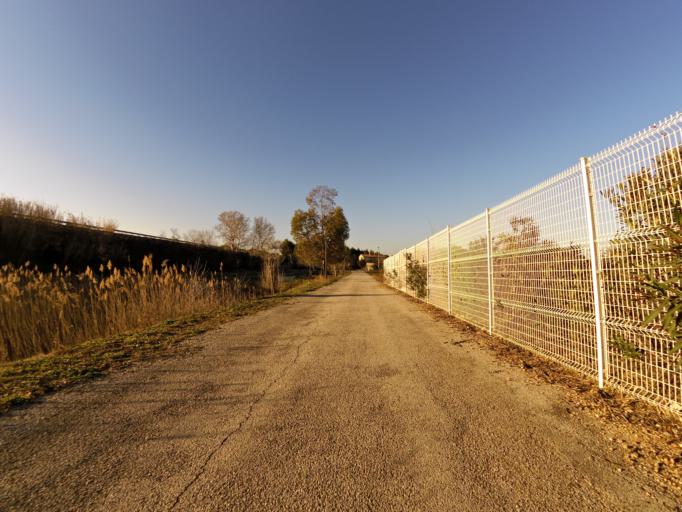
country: FR
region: Languedoc-Roussillon
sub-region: Departement du Gard
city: Gallargues-le-Montueux
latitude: 43.7200
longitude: 4.1829
